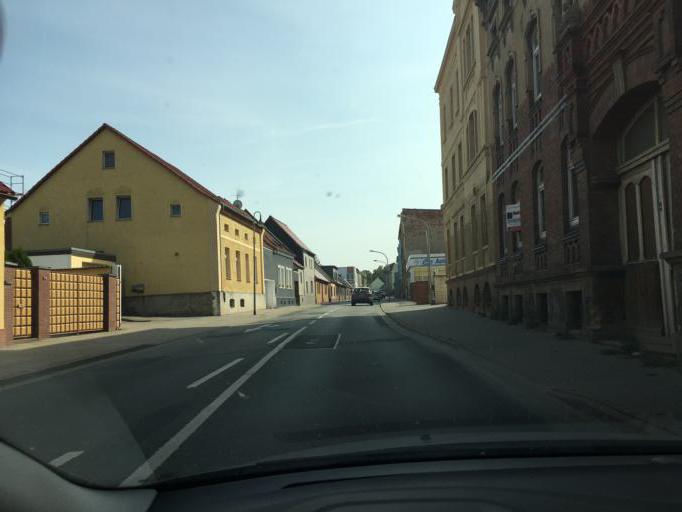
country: DE
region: Saxony-Anhalt
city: Calbe
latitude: 51.9042
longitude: 11.7712
